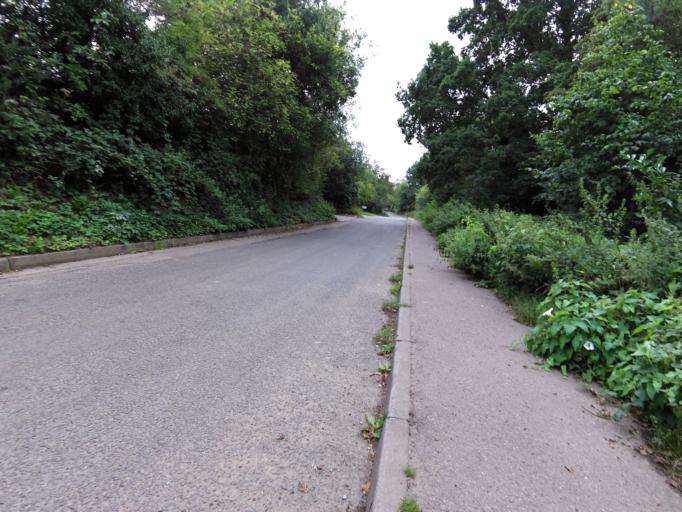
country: GB
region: England
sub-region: Hertfordshire
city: Hatfield
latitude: 51.7400
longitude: -0.2663
